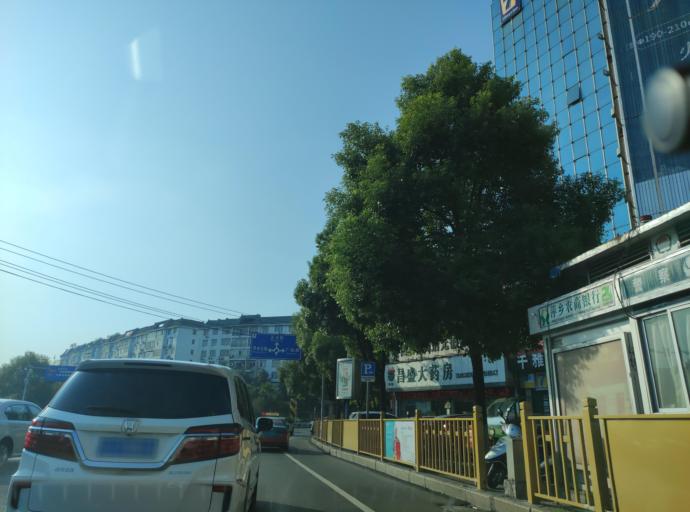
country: CN
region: Jiangxi Sheng
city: Pingxiang
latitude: 27.6297
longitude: 113.8504
